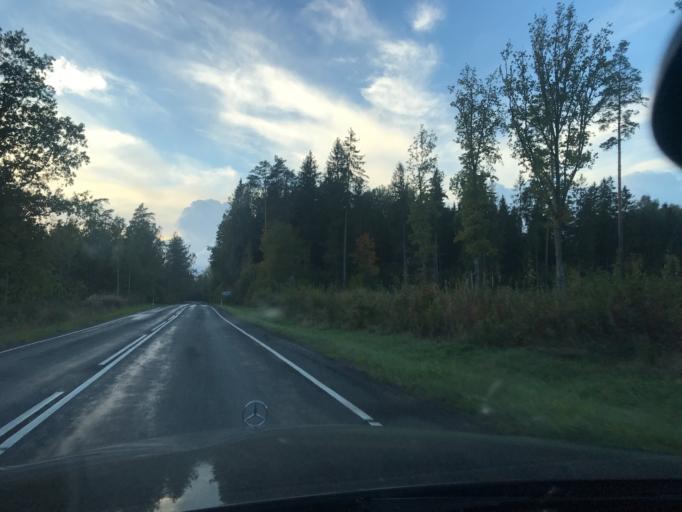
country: EE
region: Vorumaa
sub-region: Antsla vald
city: Vana-Antsla
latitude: 57.8817
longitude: 26.5714
